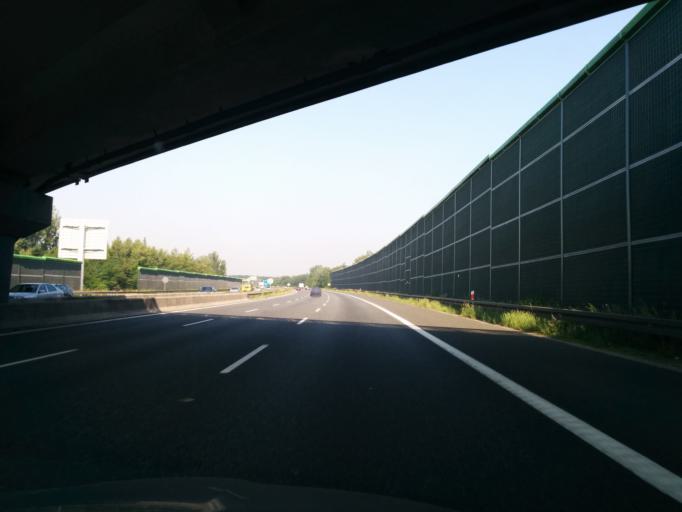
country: PL
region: Silesian Voivodeship
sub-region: Powiat gliwicki
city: Przyszowice
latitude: 50.2685
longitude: 18.7710
